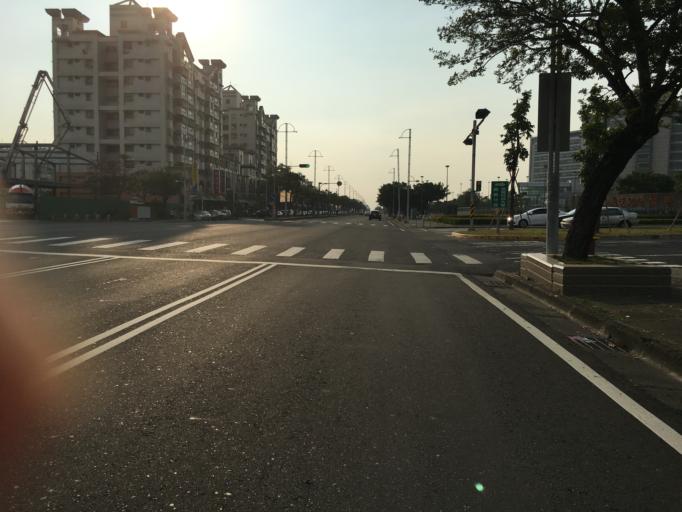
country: TW
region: Taiwan
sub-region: Chiayi
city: Taibao
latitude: 23.4610
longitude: 120.2894
